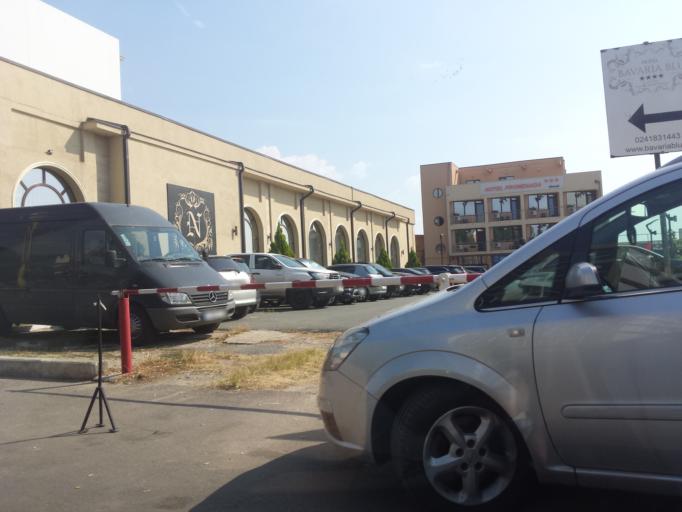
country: RO
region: Constanta
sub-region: Municipiul Constanta
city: Palazu Mare
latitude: 44.2191
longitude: 28.6358
